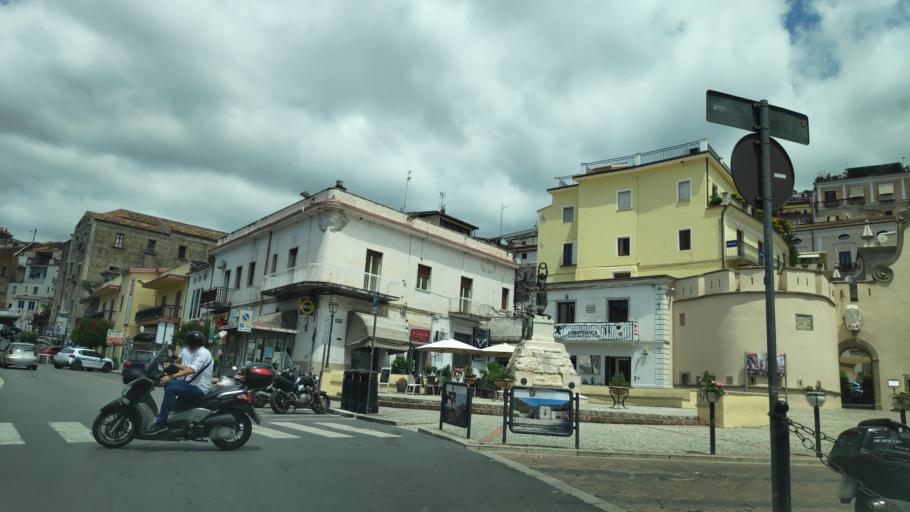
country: IT
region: Calabria
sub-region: Provincia di Cosenza
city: Paola
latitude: 39.3591
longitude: 16.0411
